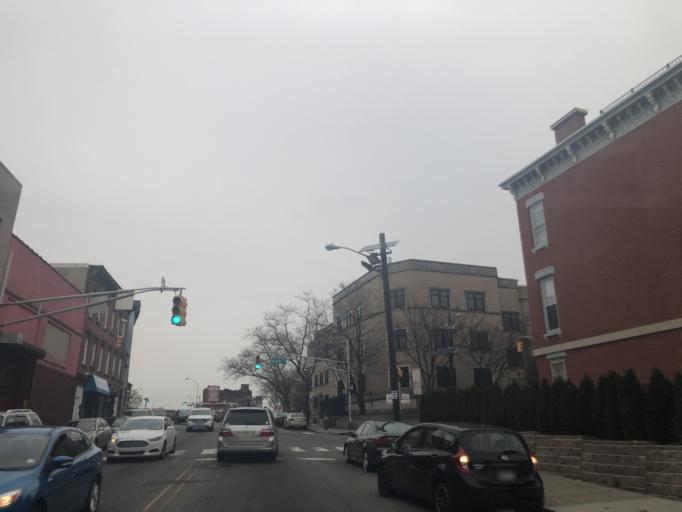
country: US
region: New Jersey
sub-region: Hudson County
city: Jersey City
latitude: 40.7159
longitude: -74.0690
